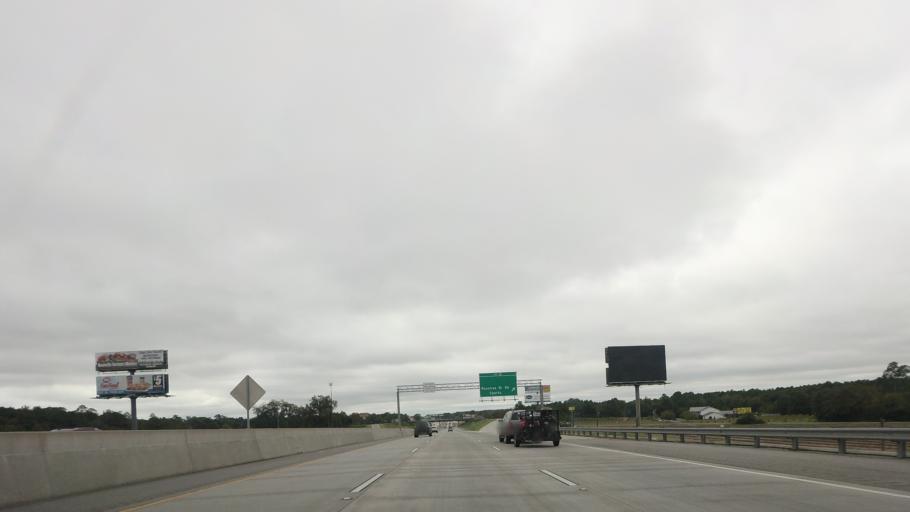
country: US
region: Georgia
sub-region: Cook County
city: Sparks
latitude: 31.1699
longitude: -83.4504
